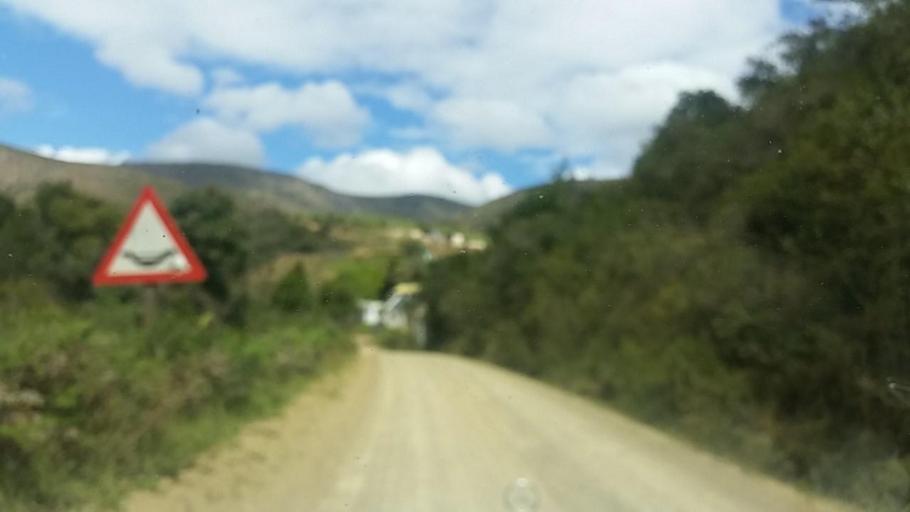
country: ZA
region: Western Cape
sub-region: Eden District Municipality
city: Knysna
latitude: -33.8110
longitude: 23.1757
